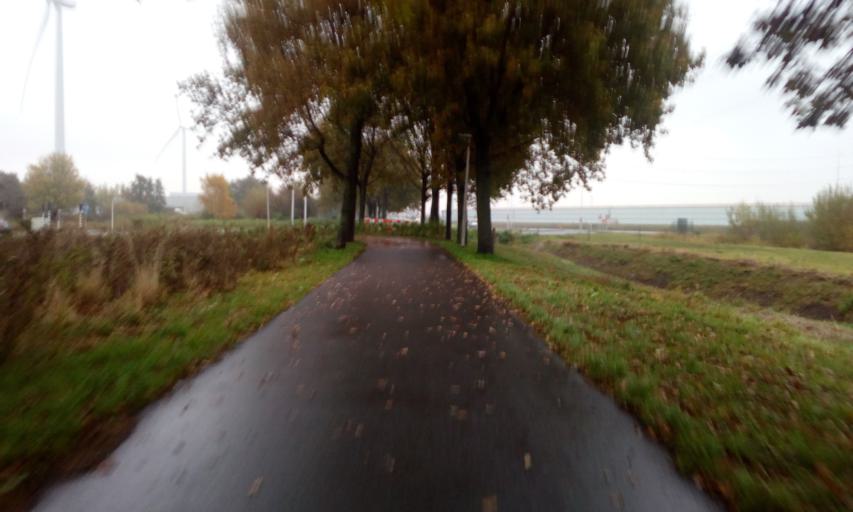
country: NL
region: South Holland
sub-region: Gemeente Zoetermeer
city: Zoetermeer
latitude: 52.0344
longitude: 4.5087
